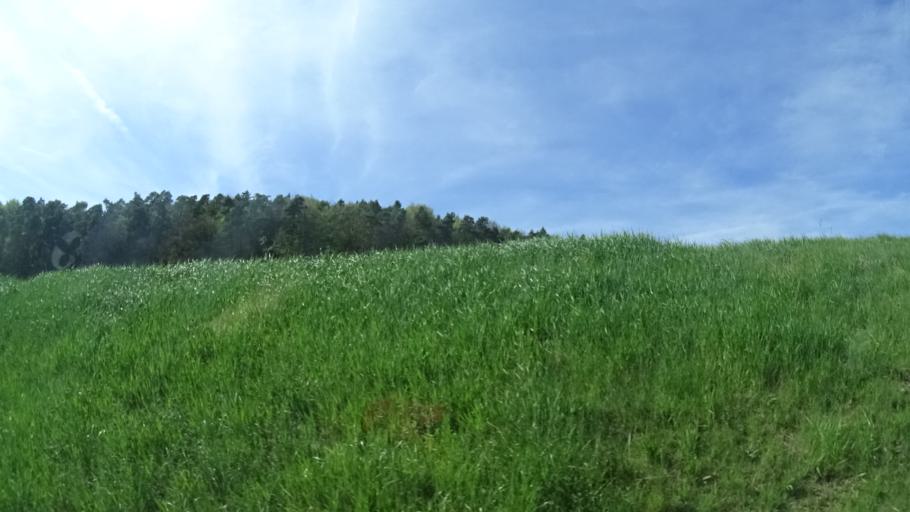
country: DE
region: Bavaria
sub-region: Regierungsbezirk Unterfranken
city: Burgpreppach
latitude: 50.1651
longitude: 10.6349
